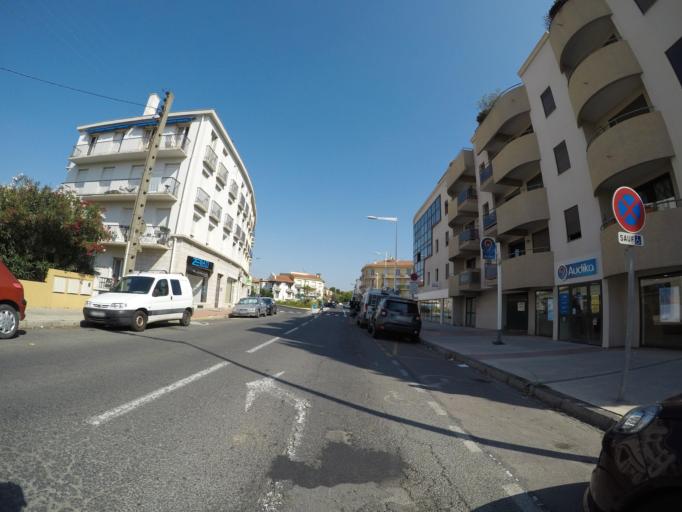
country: FR
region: Languedoc-Roussillon
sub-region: Departement des Pyrenees-Orientales
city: Perpignan
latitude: 42.6905
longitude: 2.8991
